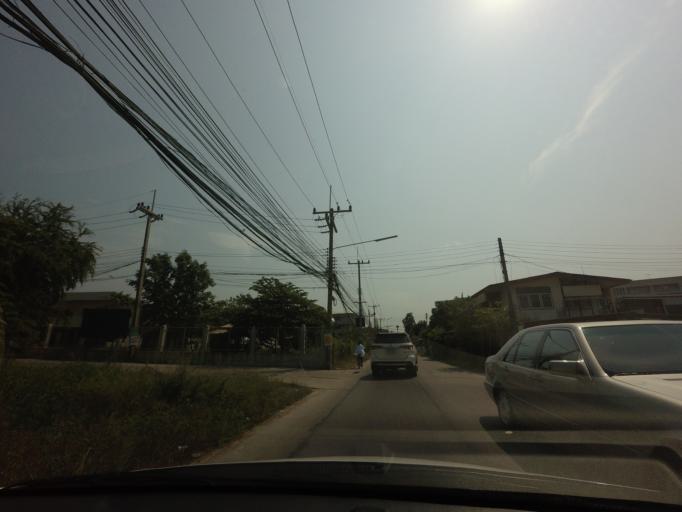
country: TH
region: Nakhon Pathom
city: Sam Phran
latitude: 13.7191
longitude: 100.2639
